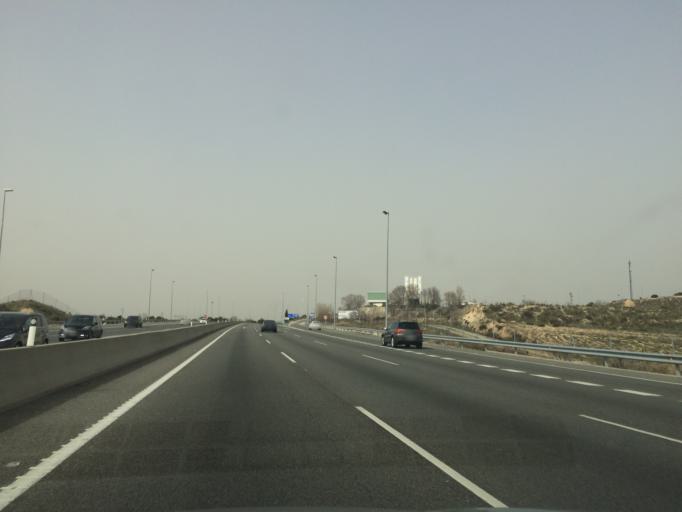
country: ES
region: Madrid
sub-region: Provincia de Madrid
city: Majadahonda
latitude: 40.4742
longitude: -3.8944
